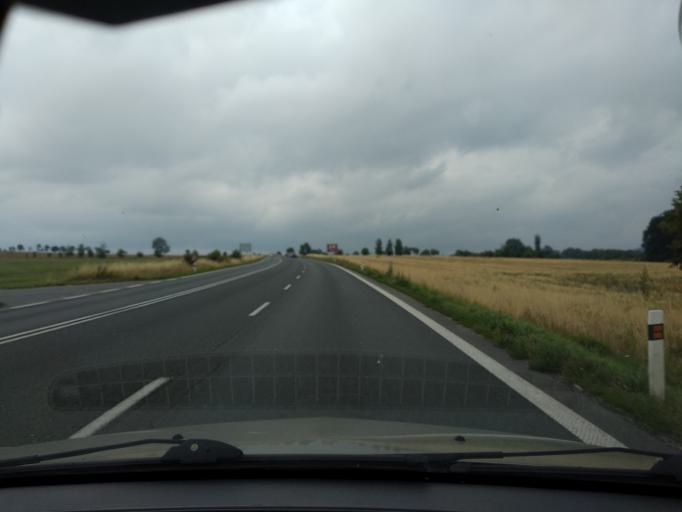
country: CZ
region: Olomoucky
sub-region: Okres Sumperk
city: Bludov
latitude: 49.9417
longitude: 16.9360
